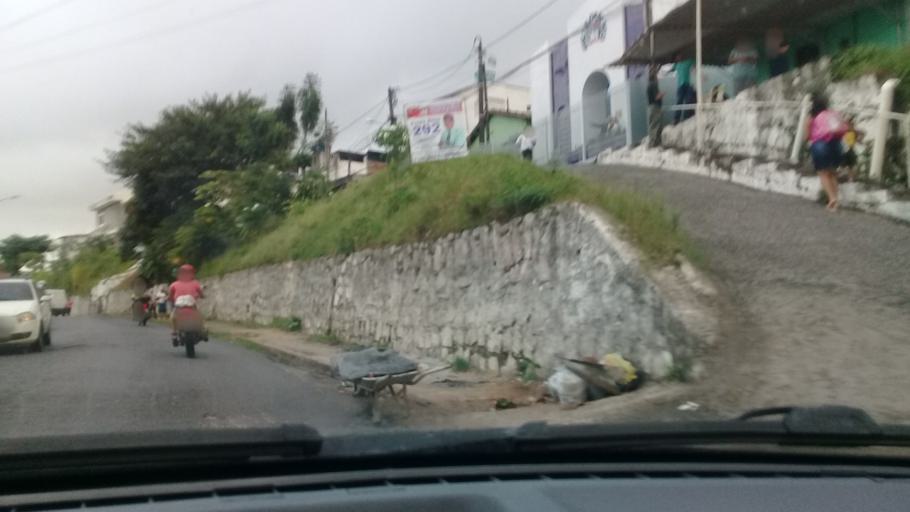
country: BR
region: Pernambuco
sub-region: Jaboatao Dos Guararapes
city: Jaboatao dos Guararapes
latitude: -8.0854
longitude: -34.9760
